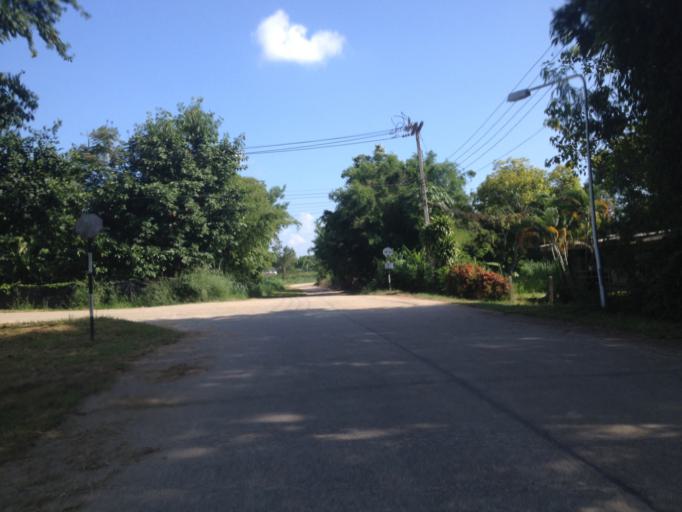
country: TH
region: Chiang Mai
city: Chiang Mai
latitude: 18.7577
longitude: 98.9279
